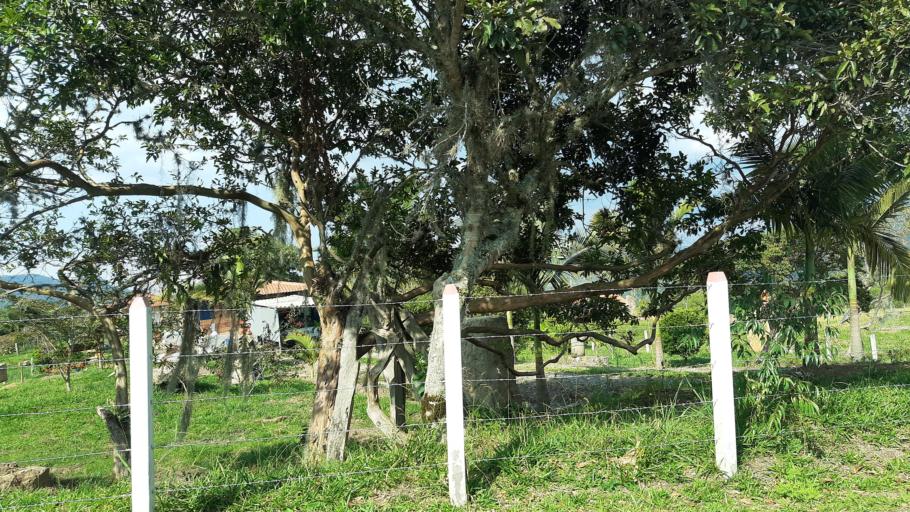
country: CO
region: Boyaca
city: Moniquira
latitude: 5.8263
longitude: -73.5935
